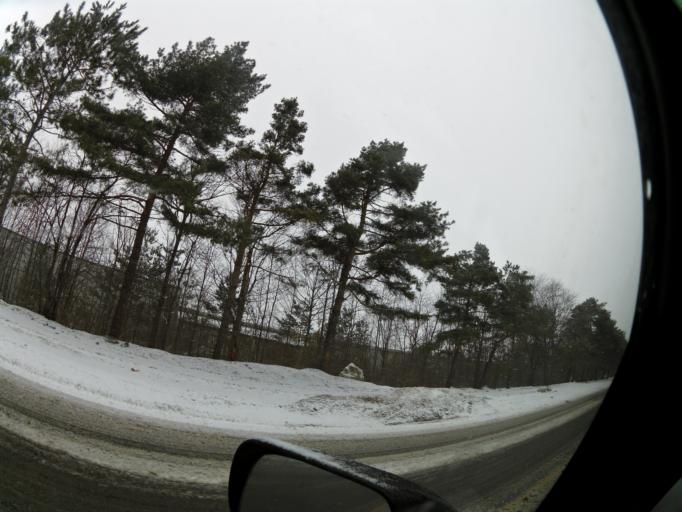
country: CA
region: Ontario
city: Ottawa
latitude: 45.4106
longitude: -75.6498
